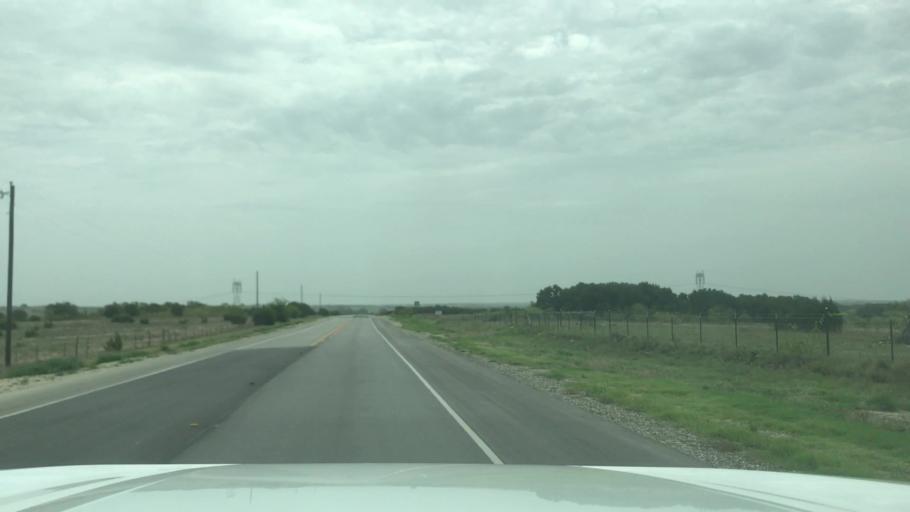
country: US
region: Texas
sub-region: Erath County
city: Dublin
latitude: 32.0784
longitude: -98.2399
